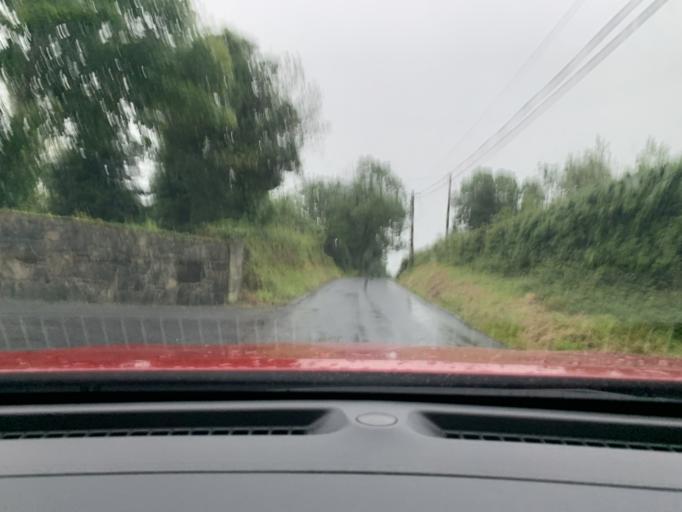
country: IE
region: Connaught
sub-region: Sligo
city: Sligo
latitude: 54.3341
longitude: -8.4119
